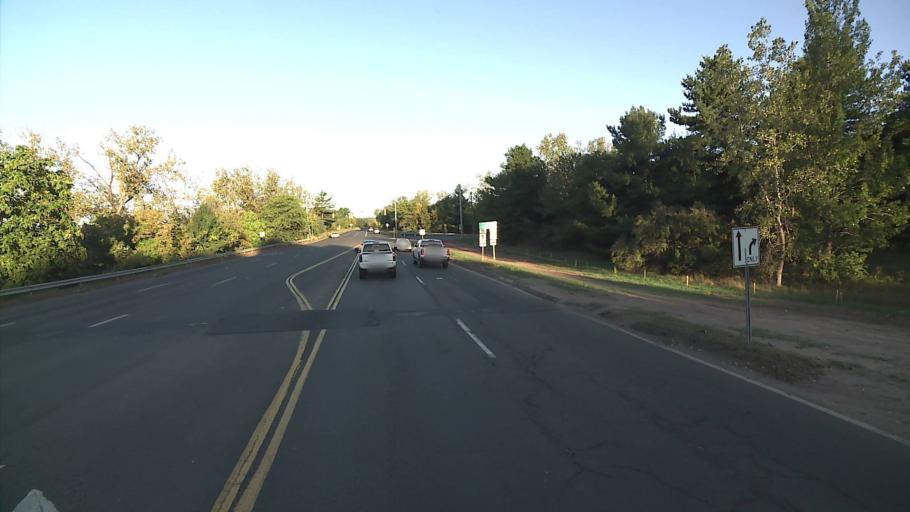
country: US
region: Connecticut
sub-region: New Haven County
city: Wallingford
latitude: 41.4850
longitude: -72.8064
